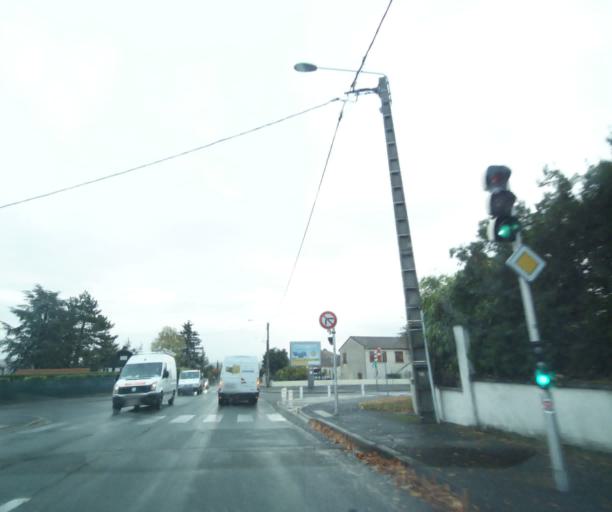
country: FR
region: Auvergne
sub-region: Departement du Puy-de-Dome
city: Cournon-d'Auvergne
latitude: 45.7350
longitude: 3.2066
